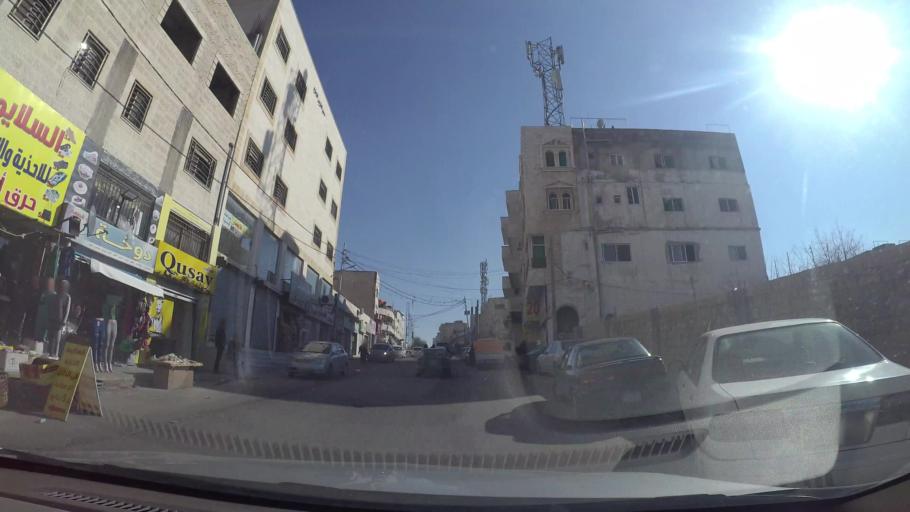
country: JO
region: Amman
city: Al Bunayyat ash Shamaliyah
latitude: 31.9069
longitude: 35.9122
